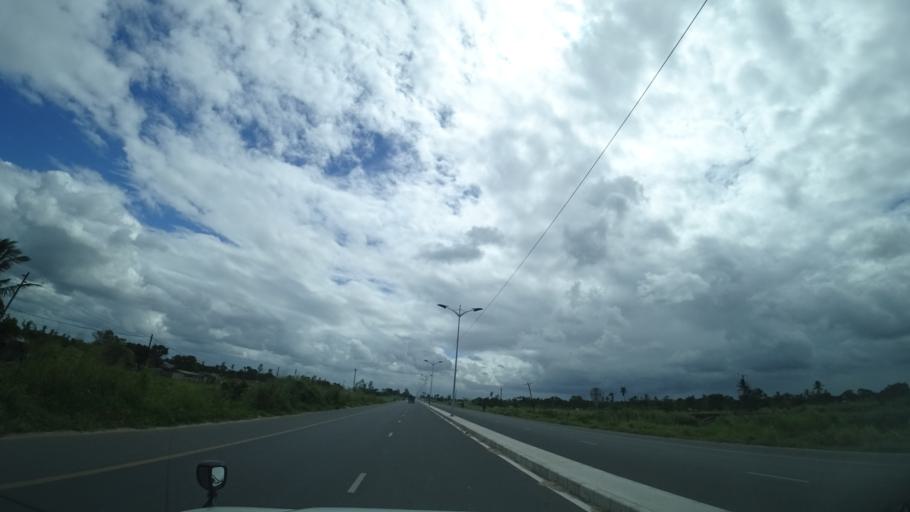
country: MZ
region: Sofala
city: Dondo
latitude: -19.6023
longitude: 34.7414
